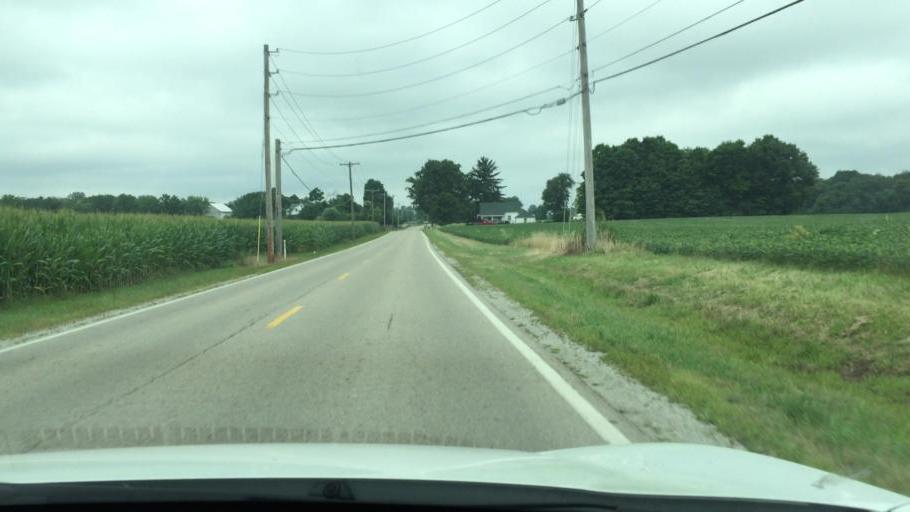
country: US
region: Ohio
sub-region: Clark County
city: Lisbon
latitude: 39.9414
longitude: -83.6498
